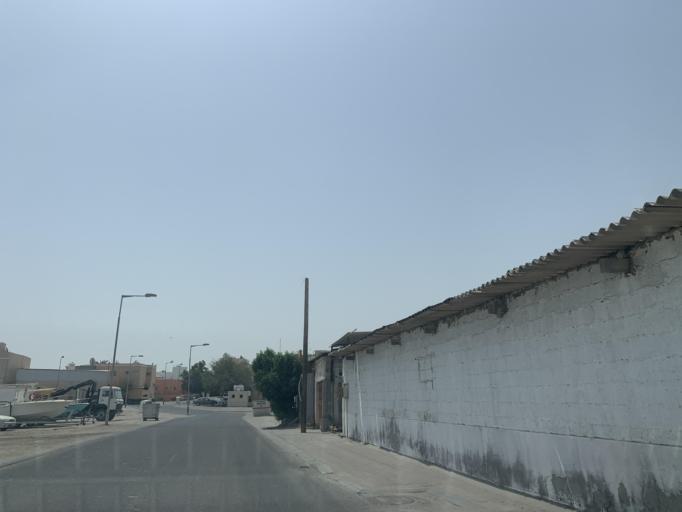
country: BH
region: Northern
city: Madinat `Isa
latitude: 26.1839
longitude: 50.5528
